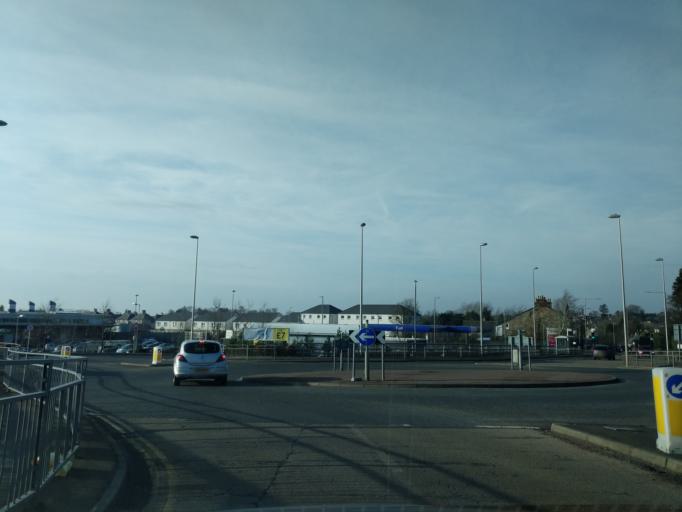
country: GB
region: Scotland
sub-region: South Lanarkshire
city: Carluke
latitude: 55.7287
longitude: -3.8355
